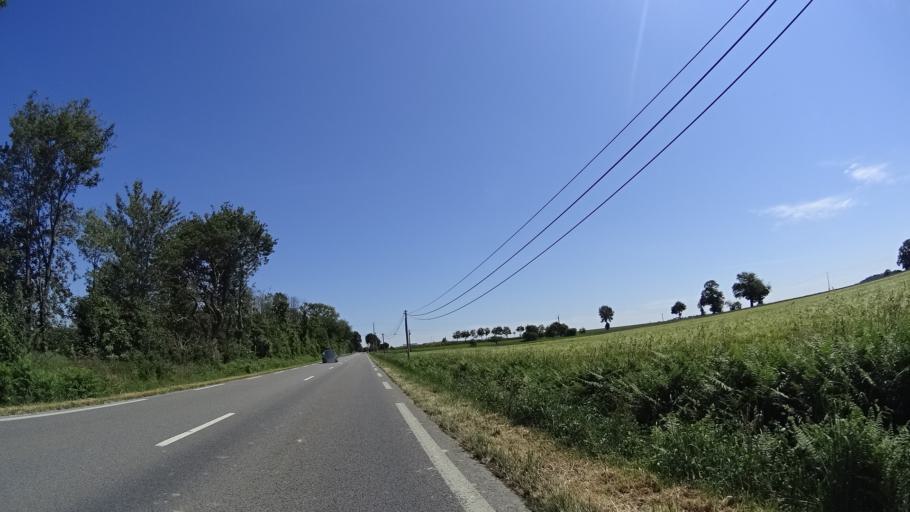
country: FR
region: Brittany
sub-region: Departement d'Ille-et-Vilaine
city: Bain-de-Bretagne
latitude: 47.8355
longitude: -1.7367
